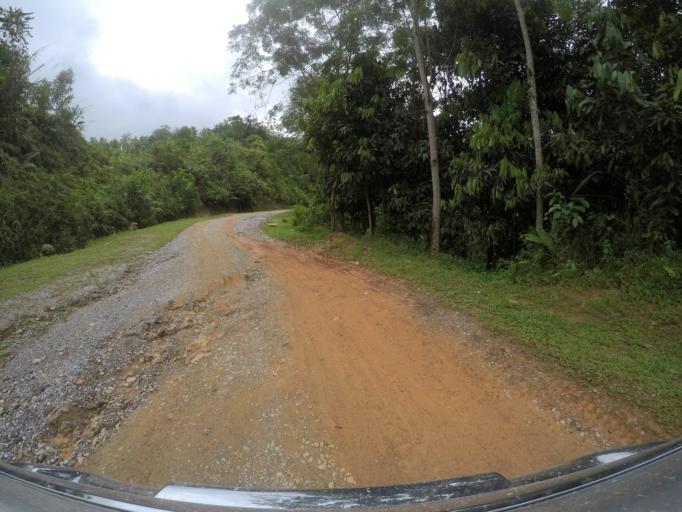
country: VN
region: Yen Bai
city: Co Phuc
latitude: 21.8122
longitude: 104.6282
